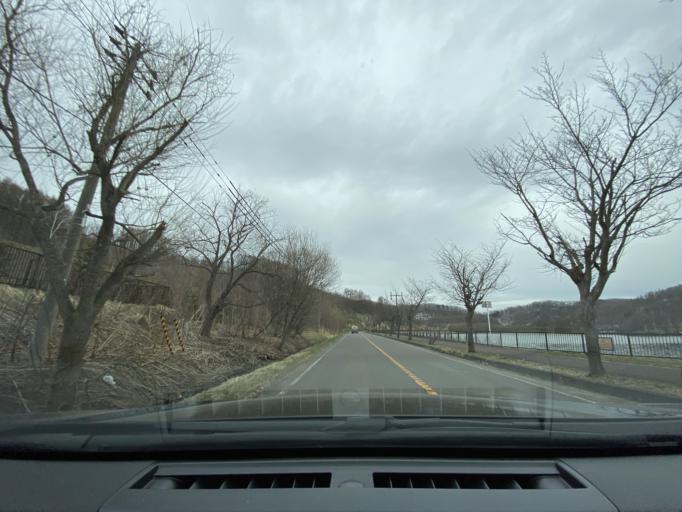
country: JP
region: Hokkaido
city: Nayoro
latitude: 44.0972
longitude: 142.4340
